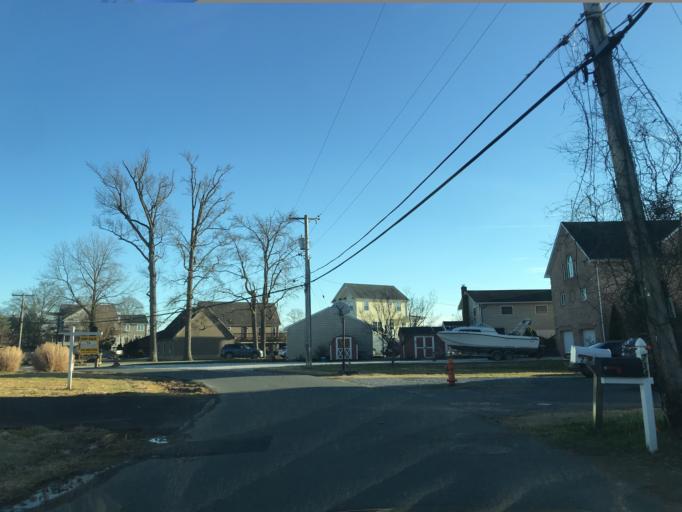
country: US
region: Maryland
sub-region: Baltimore County
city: Bowleys Quarters
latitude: 39.3237
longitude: -76.3789
